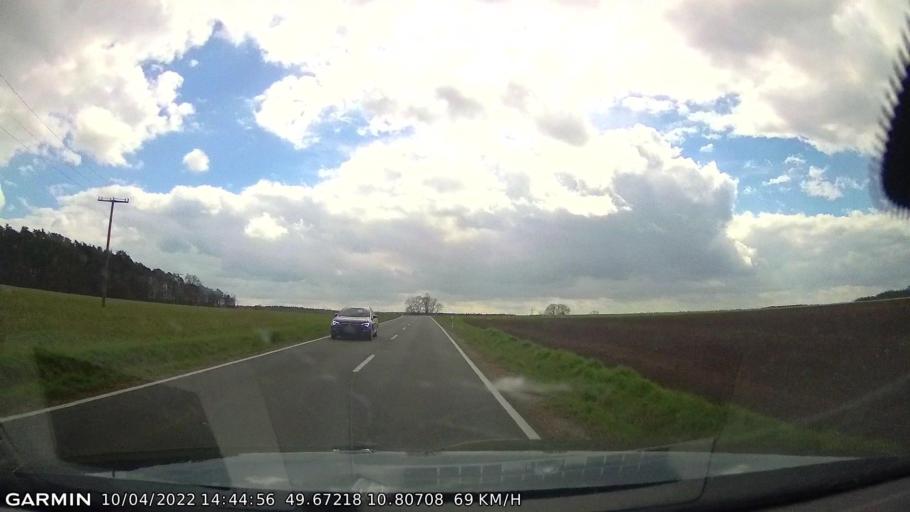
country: DE
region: Bavaria
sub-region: Regierungsbezirk Mittelfranken
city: Gremsdorf
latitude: 49.6721
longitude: 10.8070
